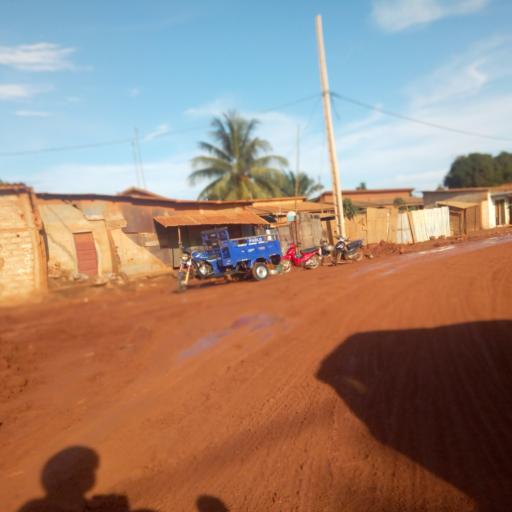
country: BJ
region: Atlantique
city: Hevie
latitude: 6.4190
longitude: 2.2616
